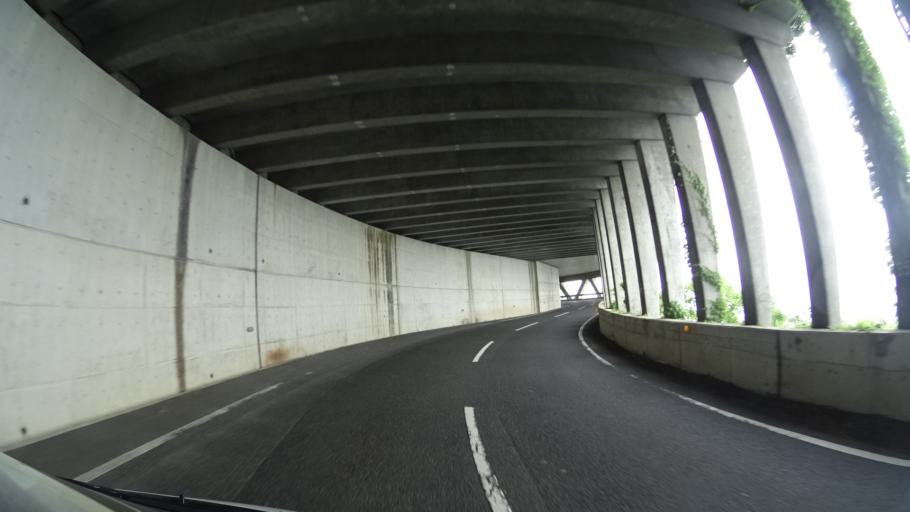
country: JP
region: Kyoto
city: Miyazu
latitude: 35.7597
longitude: 135.2427
